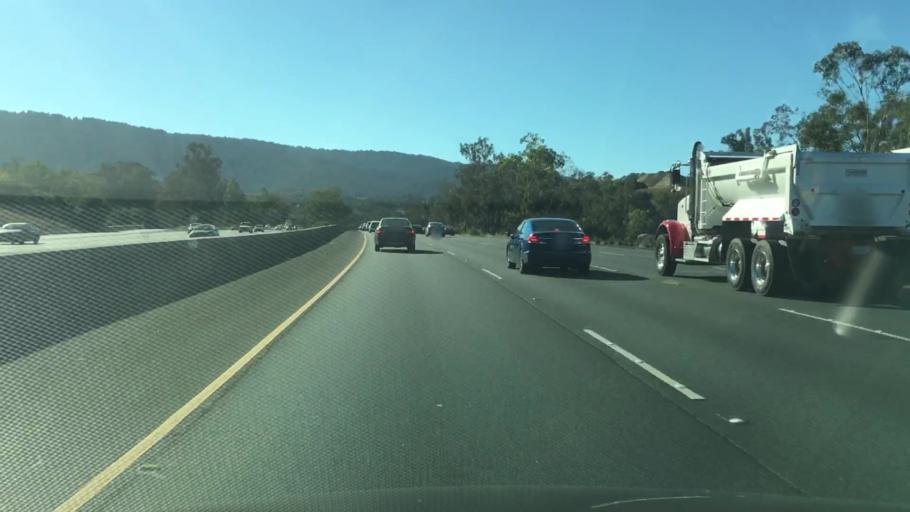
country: US
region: California
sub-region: San Mateo County
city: Woodside
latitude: 37.4434
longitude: -122.2595
